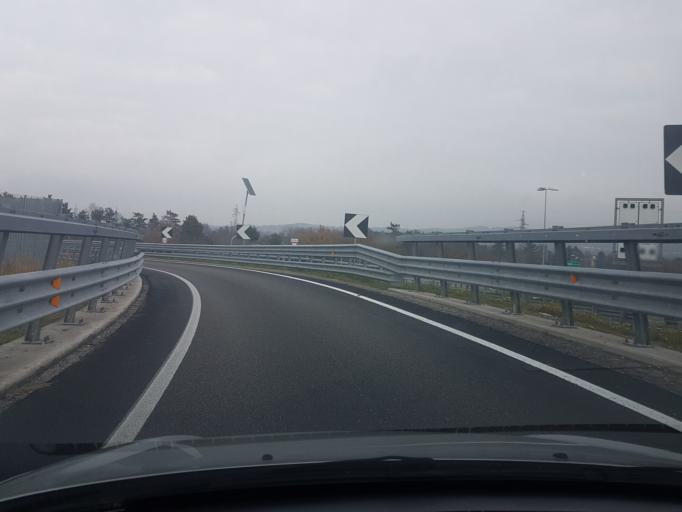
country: IT
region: Friuli Venezia Giulia
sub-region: Provincia di Trieste
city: Trieste
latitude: 45.6590
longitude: 13.8323
